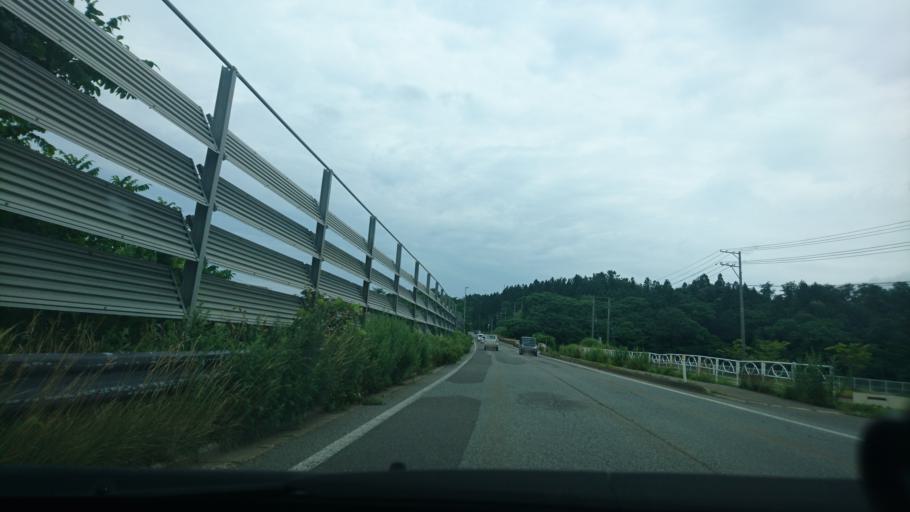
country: JP
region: Akita
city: Yokotemachi
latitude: 39.3329
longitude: 140.5590
